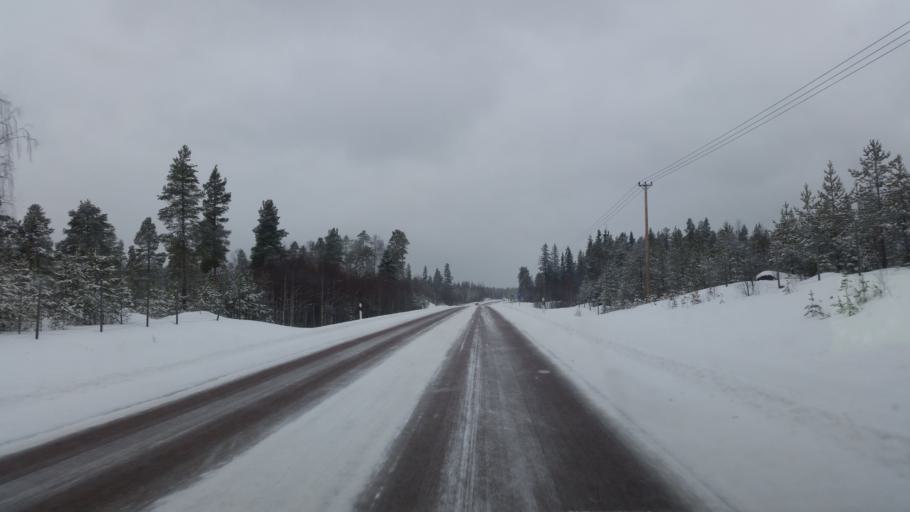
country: SE
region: Jaemtland
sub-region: Harjedalens Kommun
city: Sveg
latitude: 62.2378
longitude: 14.8335
